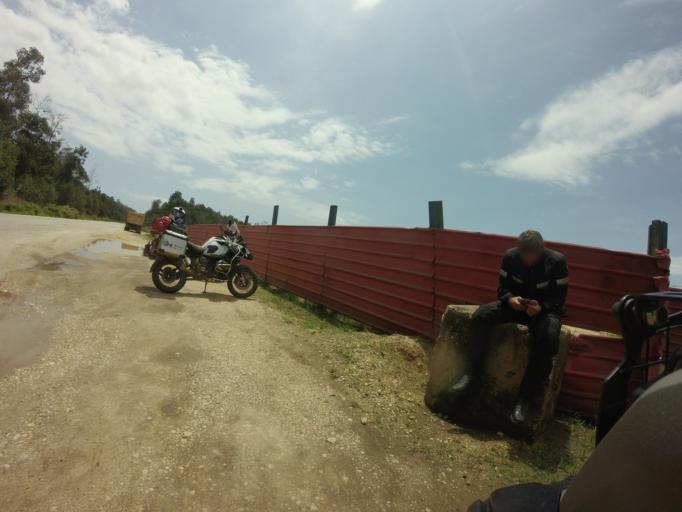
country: AO
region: Cabinda
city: Cabinda
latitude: -5.2130
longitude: 12.1440
